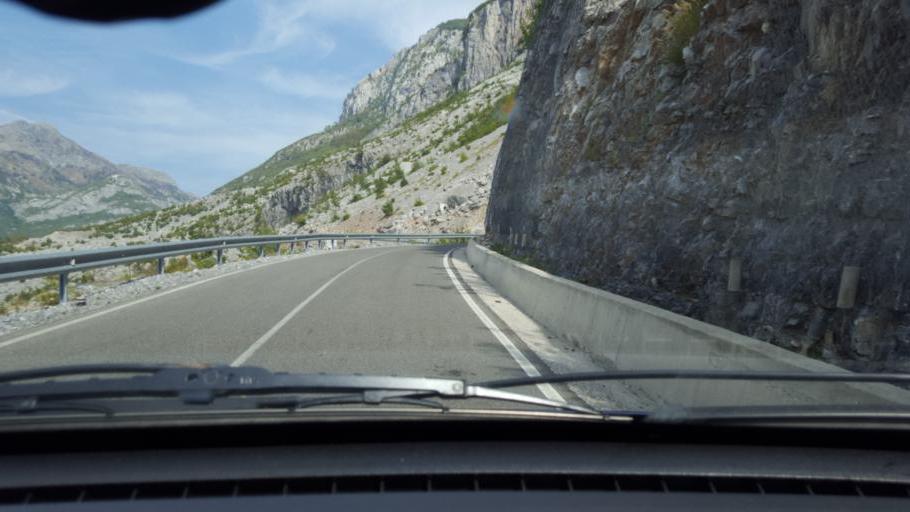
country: AL
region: Shkoder
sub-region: Rrethi i Malesia e Madhe
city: Kastrat
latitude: 42.5052
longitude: 19.6123
